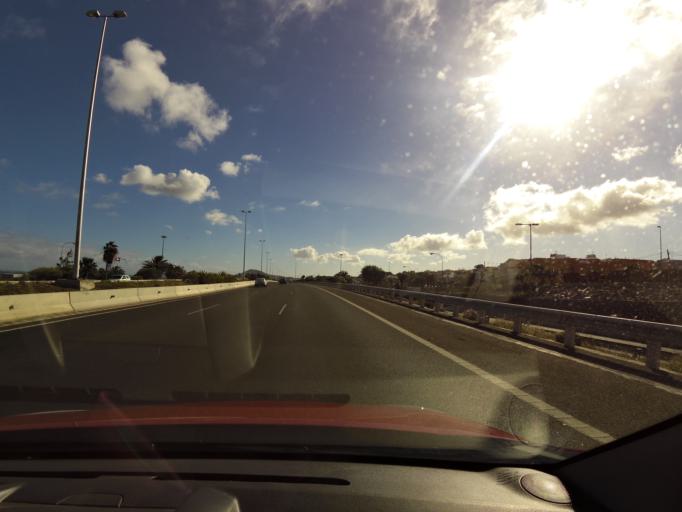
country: ES
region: Canary Islands
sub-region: Provincia de Las Palmas
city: Ingenio
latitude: 27.9226
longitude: -15.3982
